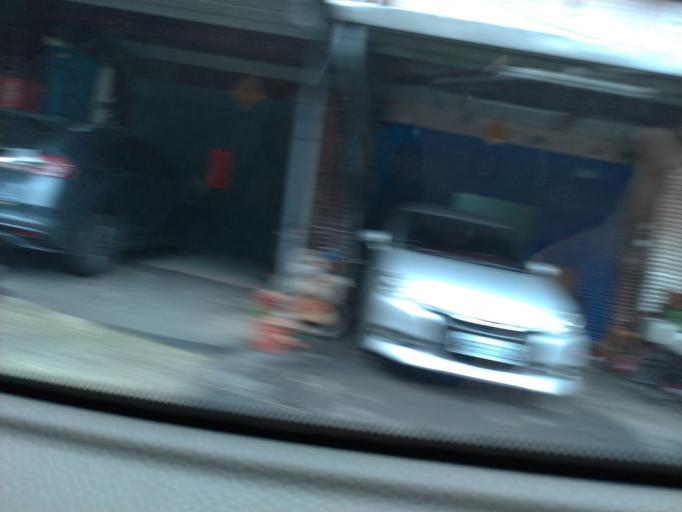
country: TW
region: Taipei
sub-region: Taipei
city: Banqiao
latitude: 24.9303
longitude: 121.4105
